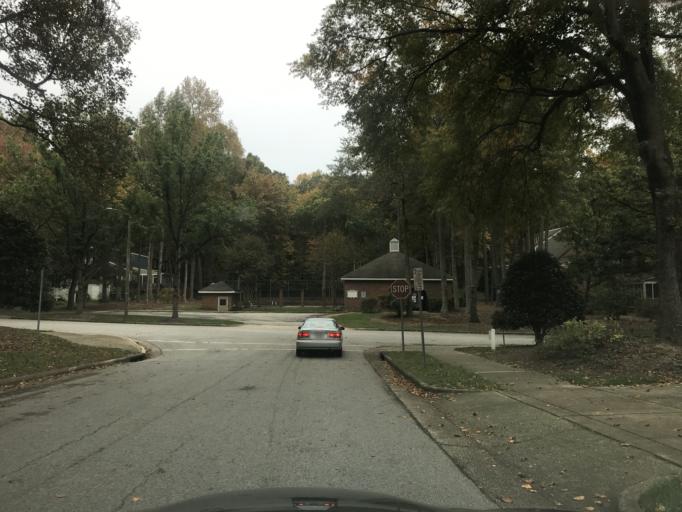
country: US
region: North Carolina
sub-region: Wake County
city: West Raleigh
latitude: 35.8897
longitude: -78.6307
